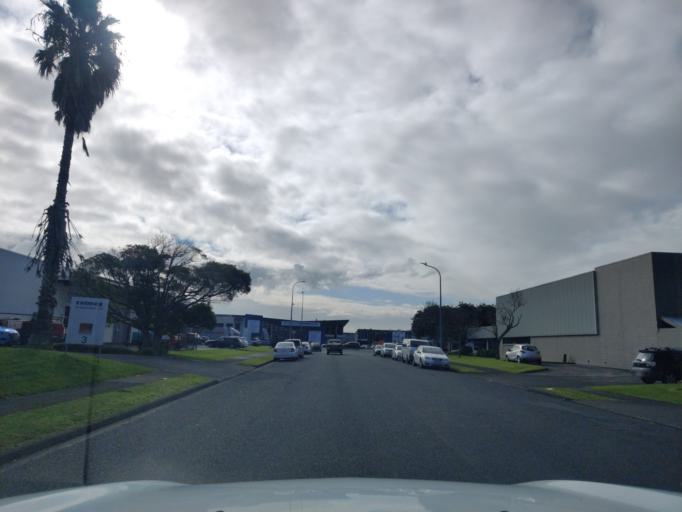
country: NZ
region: Auckland
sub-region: Auckland
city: Manukau City
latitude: -36.9386
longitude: 174.8822
